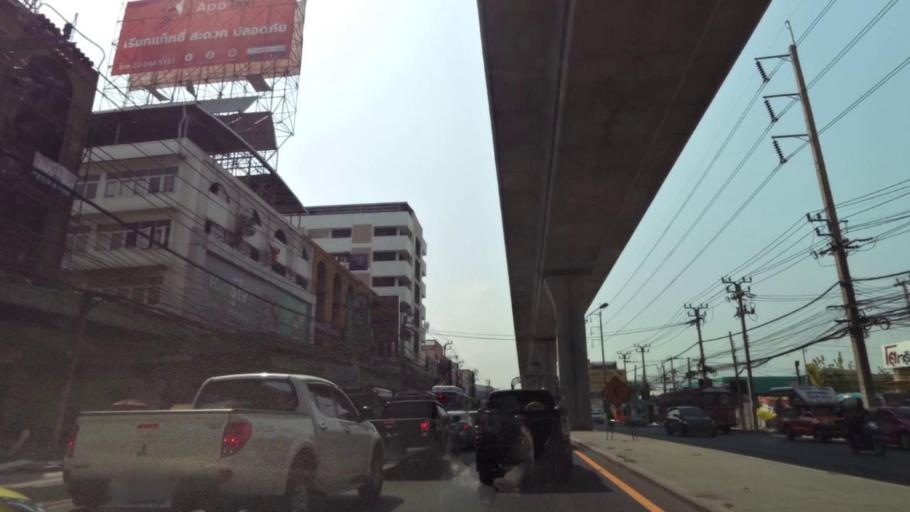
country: TH
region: Bangkok
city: Bang Na
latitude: 13.6582
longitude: 100.6006
